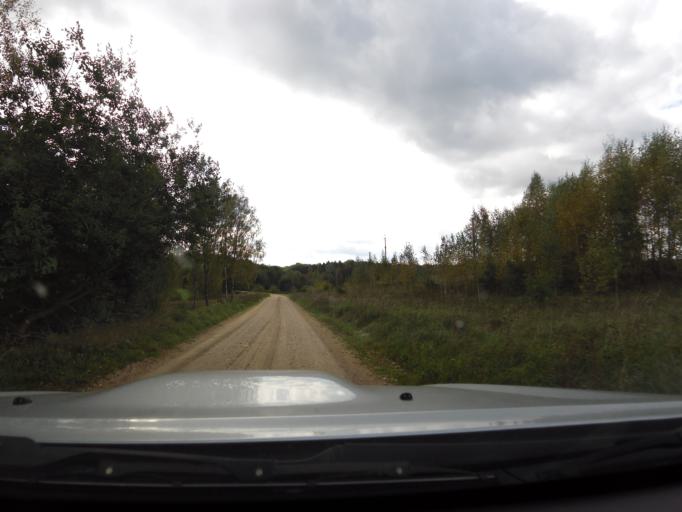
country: LT
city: Grigiskes
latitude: 54.7768
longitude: 25.0639
